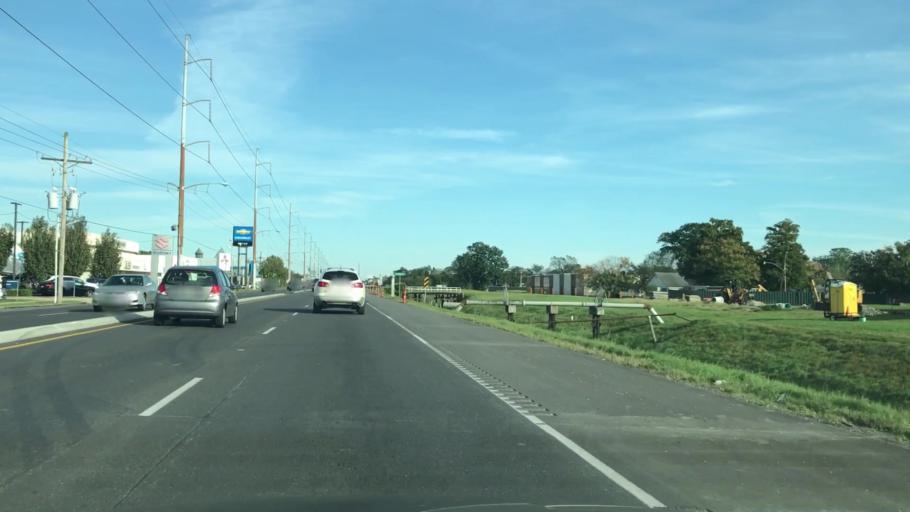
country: US
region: Louisiana
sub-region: Jefferson Parish
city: Kenner
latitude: 29.9789
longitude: -90.2296
